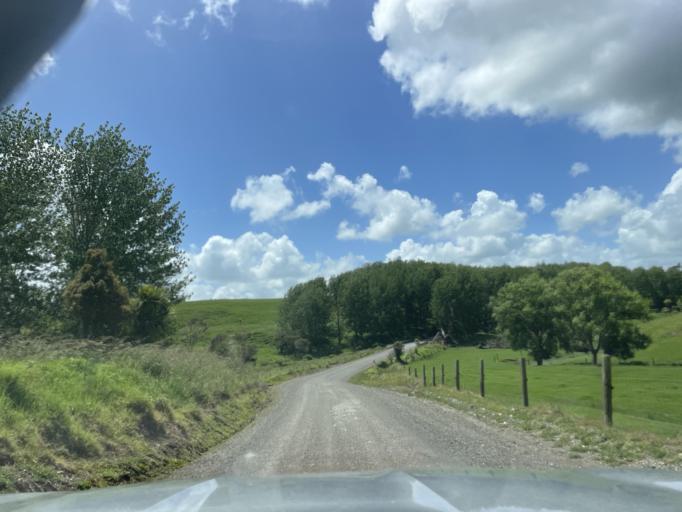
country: NZ
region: Auckland
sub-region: Auckland
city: Wellsford
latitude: -36.1776
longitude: 174.3151
